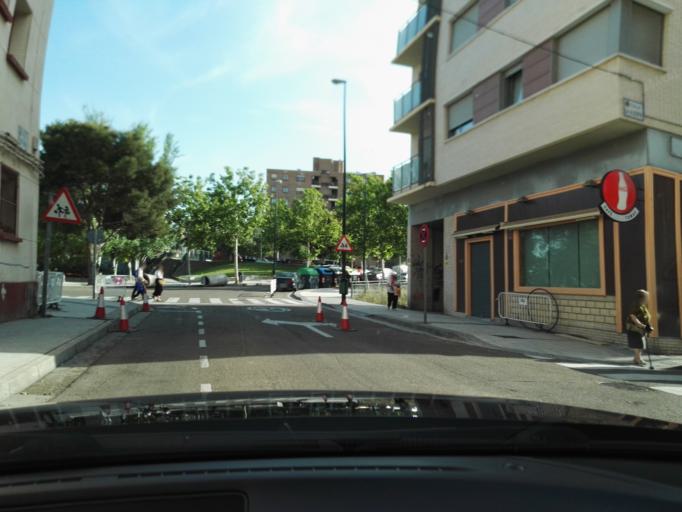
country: ES
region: Aragon
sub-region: Provincia de Zaragoza
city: Zaragoza
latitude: 41.6363
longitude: -0.8724
